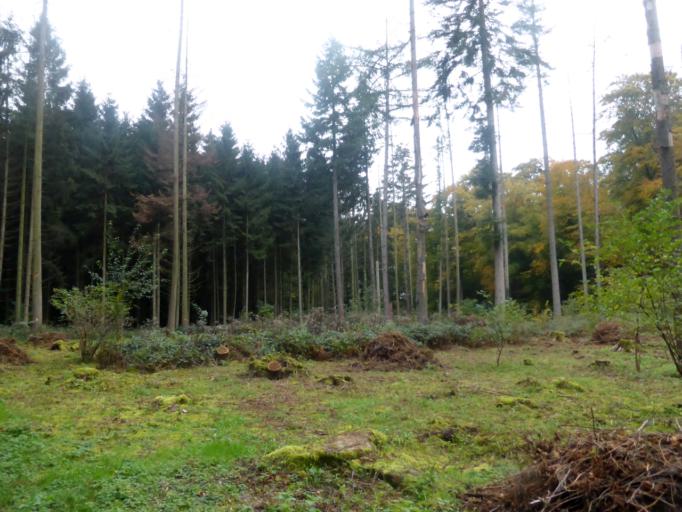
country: LU
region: Luxembourg
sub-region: Canton d'Esch-sur-Alzette
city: Leudelange
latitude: 49.5480
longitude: 6.0637
